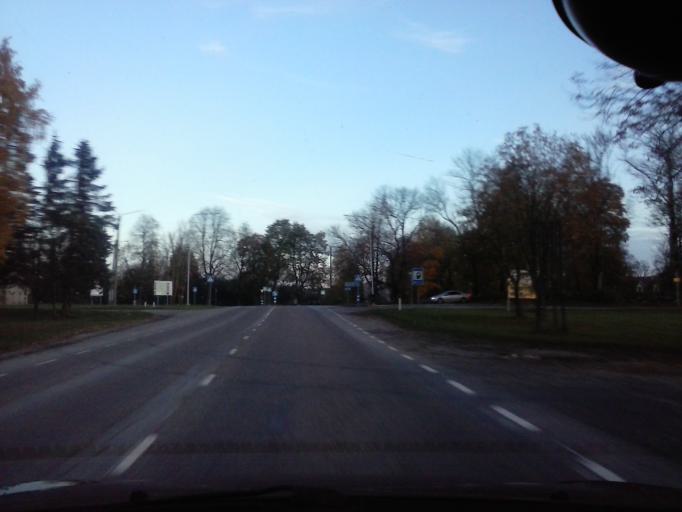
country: EE
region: Raplamaa
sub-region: Maerjamaa vald
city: Marjamaa
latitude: 58.9120
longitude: 24.4309
